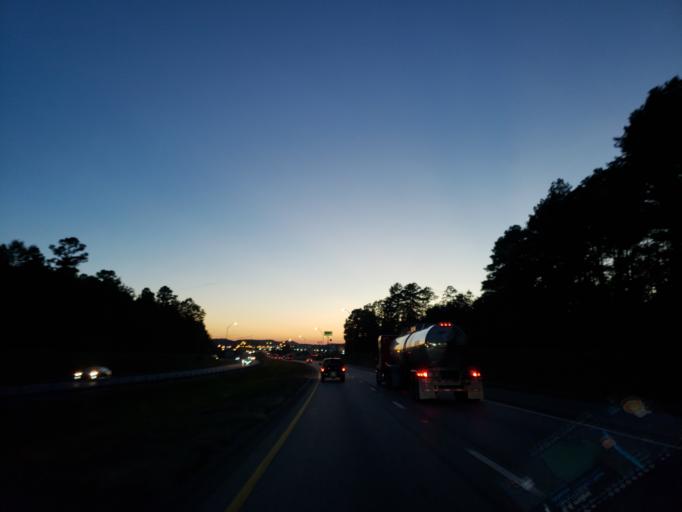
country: US
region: Mississippi
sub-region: Lauderdale County
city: Meridian
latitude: 32.3728
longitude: -88.6675
